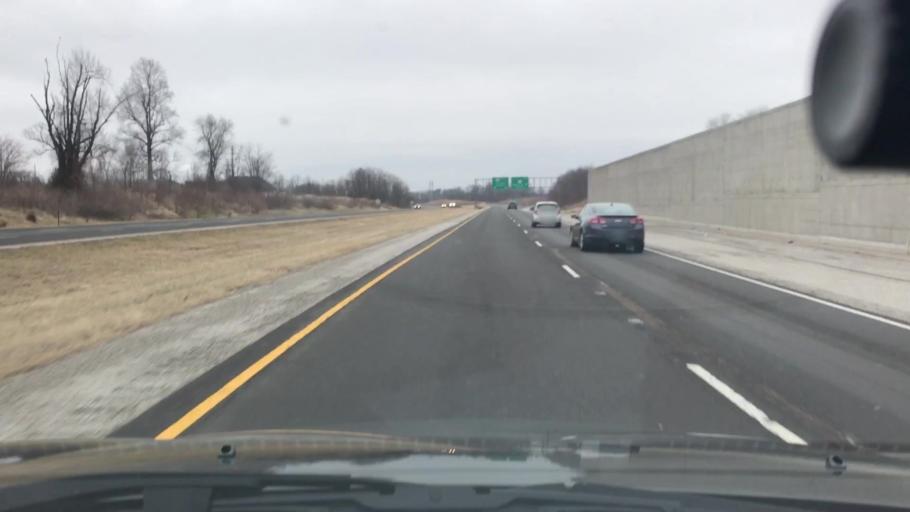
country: US
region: Illinois
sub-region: Madison County
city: Rosewood Heights
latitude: 38.8798
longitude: -90.0596
